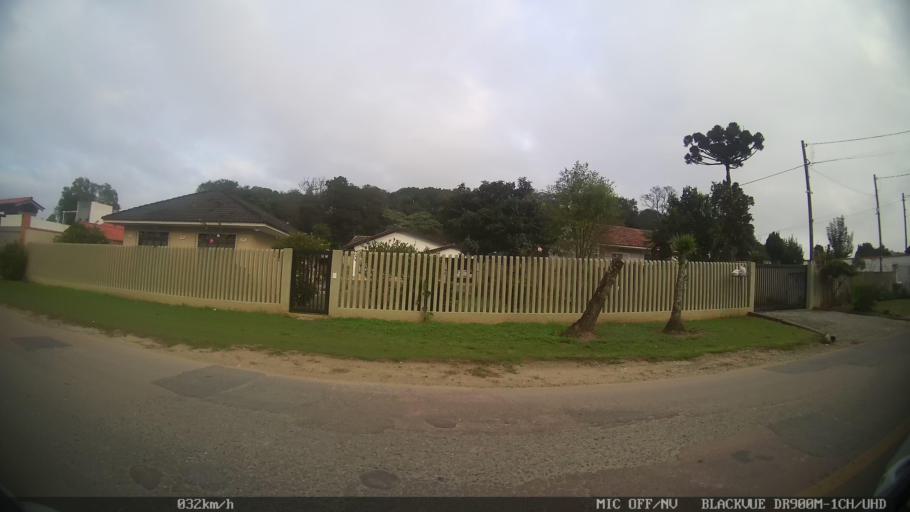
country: BR
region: Parana
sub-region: Almirante Tamandare
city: Almirante Tamandare
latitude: -25.3890
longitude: -49.3383
